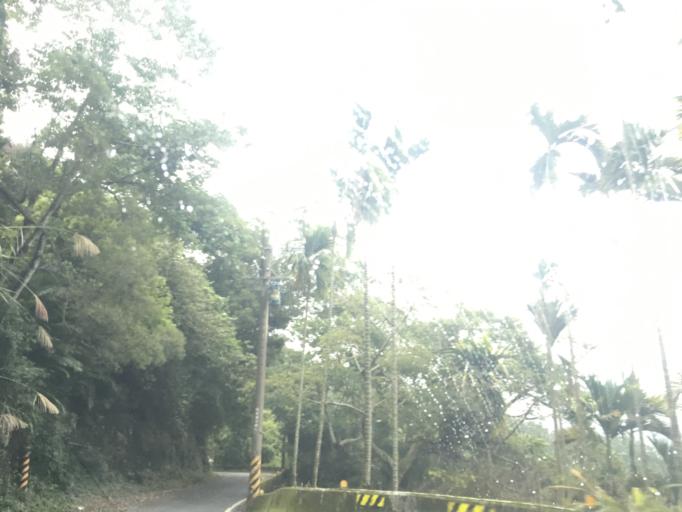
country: TW
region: Taiwan
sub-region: Yunlin
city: Douliu
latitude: 23.5633
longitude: 120.6140
